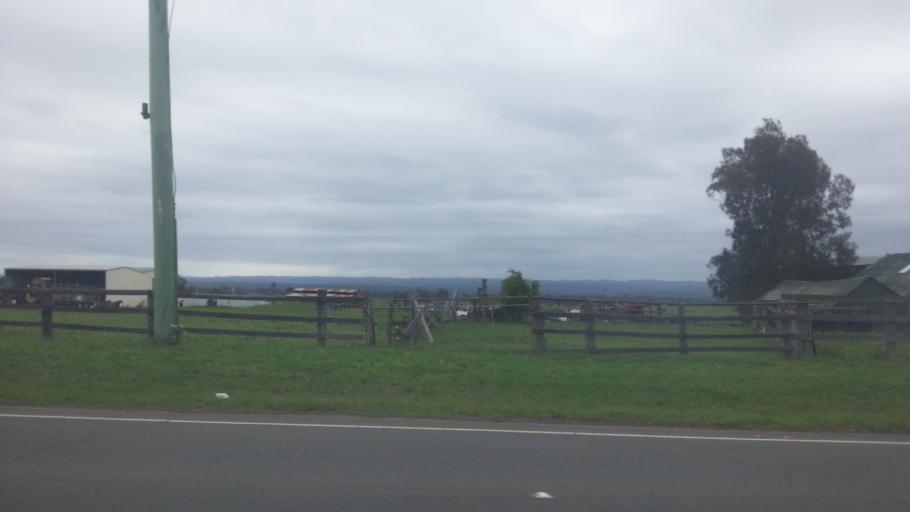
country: AU
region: New South Wales
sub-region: Liverpool
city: Luddenham
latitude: -33.8611
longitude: 150.6980
